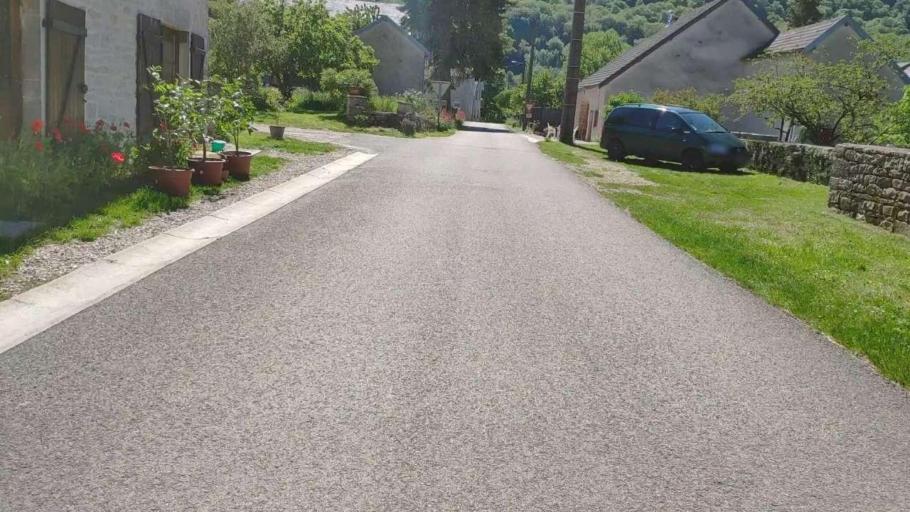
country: FR
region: Franche-Comte
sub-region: Departement du Jura
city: Poligny
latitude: 46.7281
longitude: 5.7476
